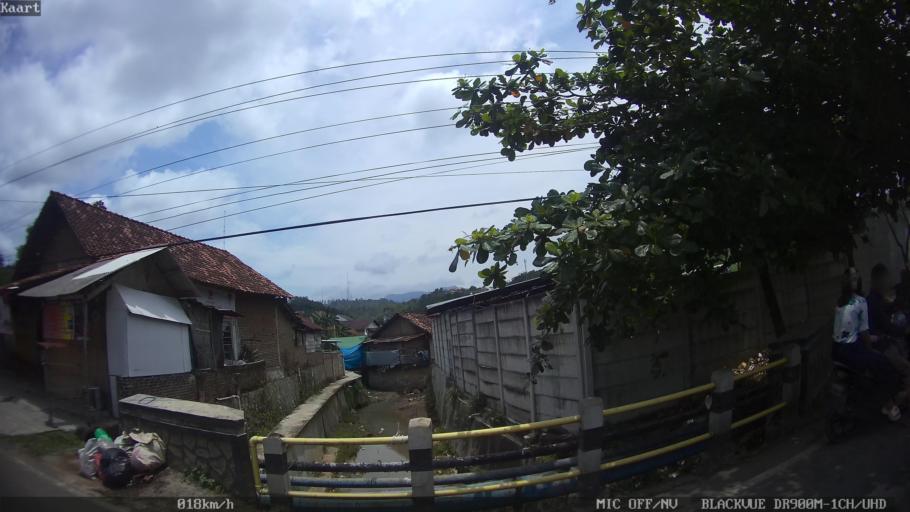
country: ID
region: Lampung
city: Bandarlampung
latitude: -5.4116
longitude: 105.2447
